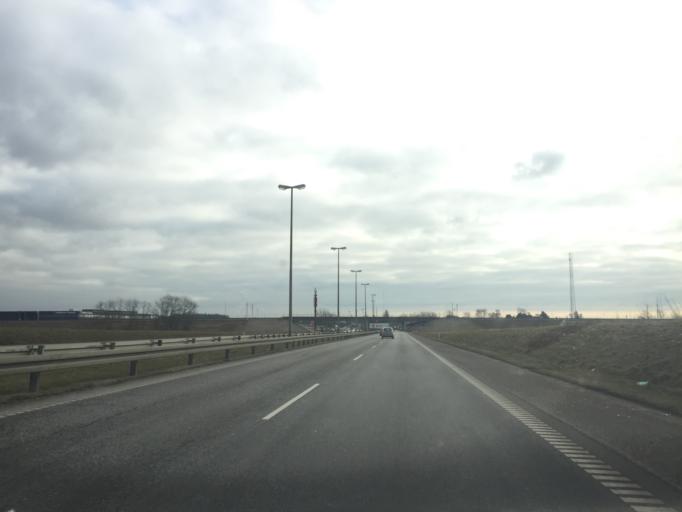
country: DK
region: Capital Region
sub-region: Hoje-Taastrup Kommune
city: Taastrup
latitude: 55.6246
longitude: 12.3156
